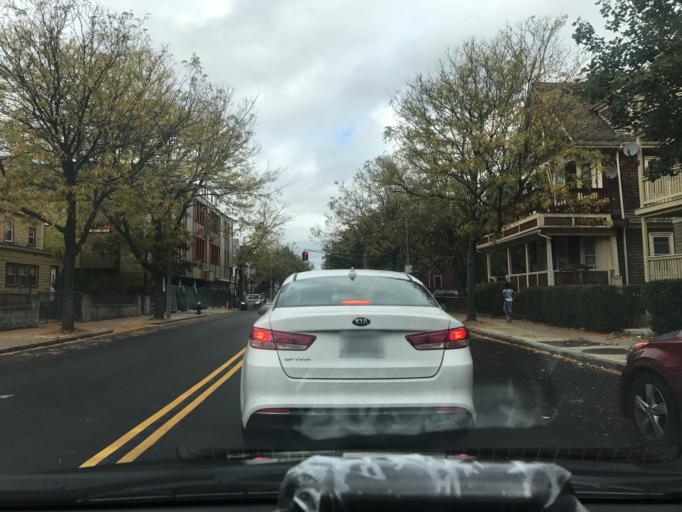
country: US
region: Massachusetts
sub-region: Norfolk County
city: Milton
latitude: 42.2857
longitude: -71.0712
